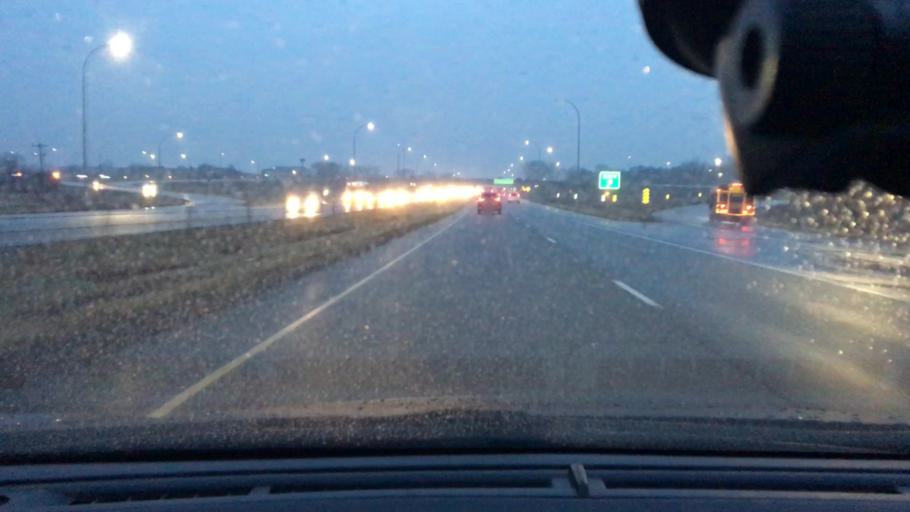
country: US
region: Minnesota
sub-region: Hennepin County
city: New Hope
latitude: 45.0298
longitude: -93.4006
